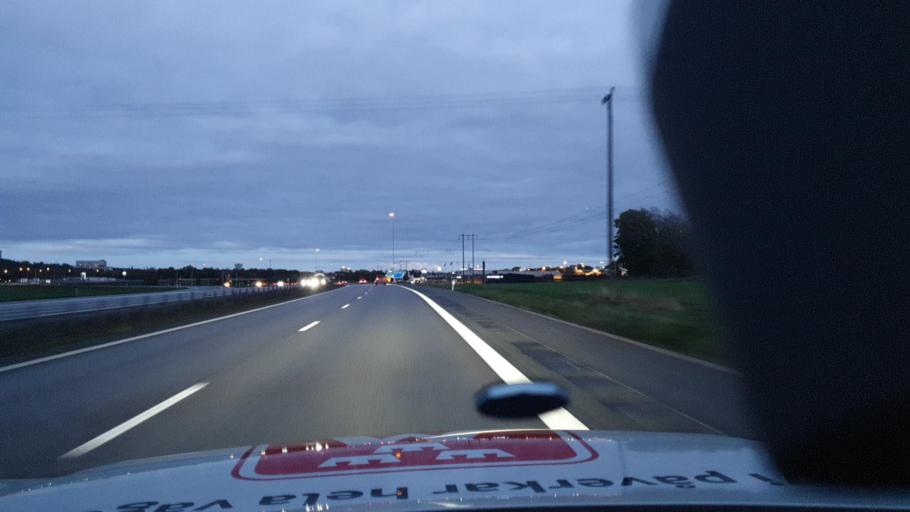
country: SE
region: Soedermanland
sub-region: Nykopings Kommun
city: Nykoping
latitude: 58.7485
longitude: 16.9636
